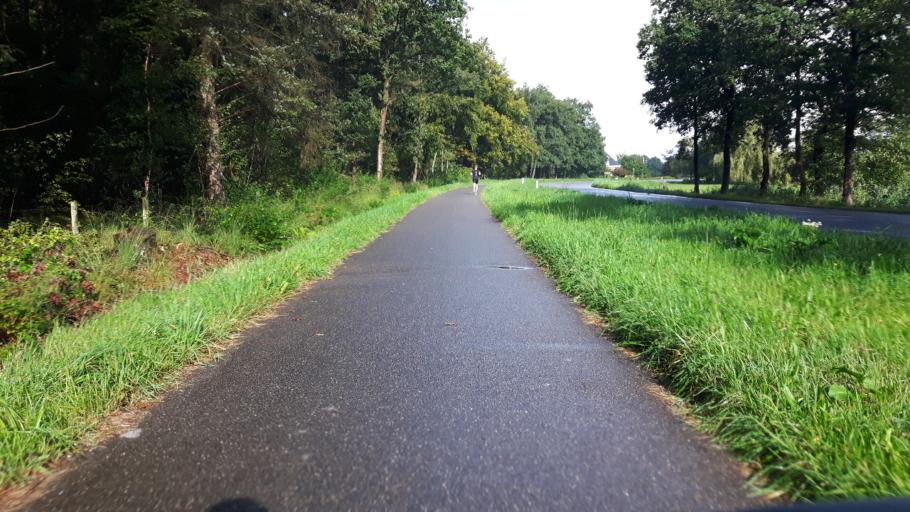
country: NL
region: Friesland
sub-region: Gemeente Smallingerland
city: Drachten
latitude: 53.0733
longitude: 6.0991
